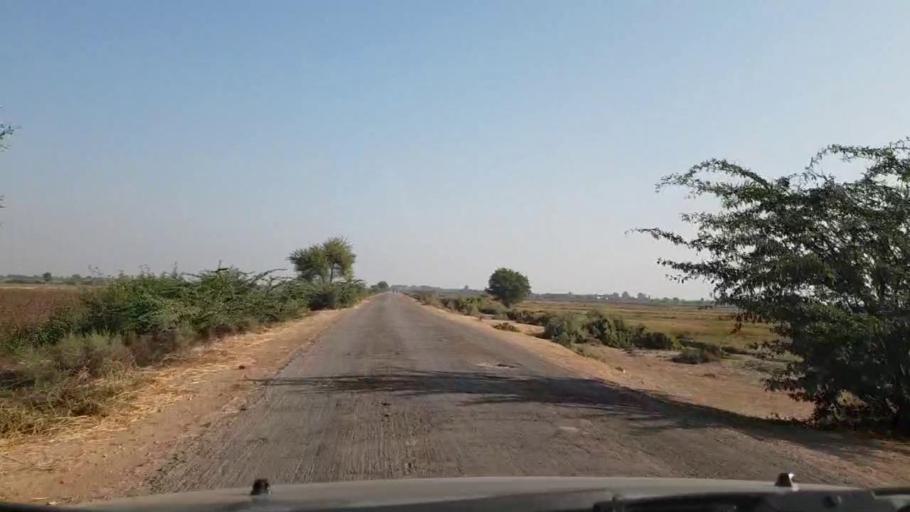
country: PK
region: Sindh
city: Tando Bago
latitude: 24.8621
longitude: 69.0478
